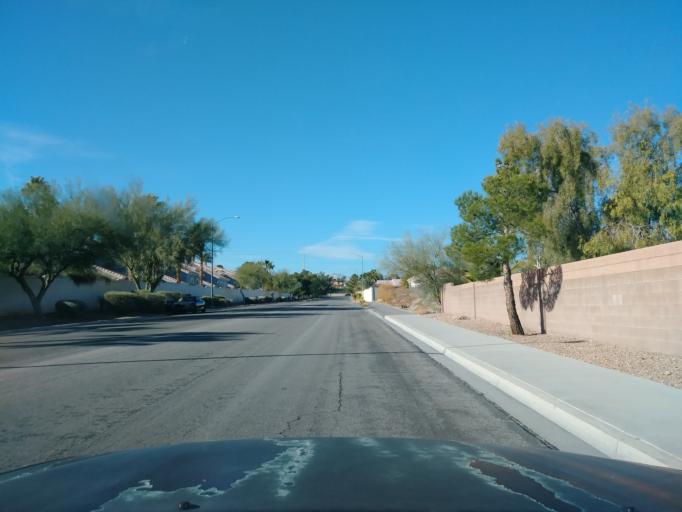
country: US
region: Nevada
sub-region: Clark County
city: Spring Valley
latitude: 36.1459
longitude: -115.2749
